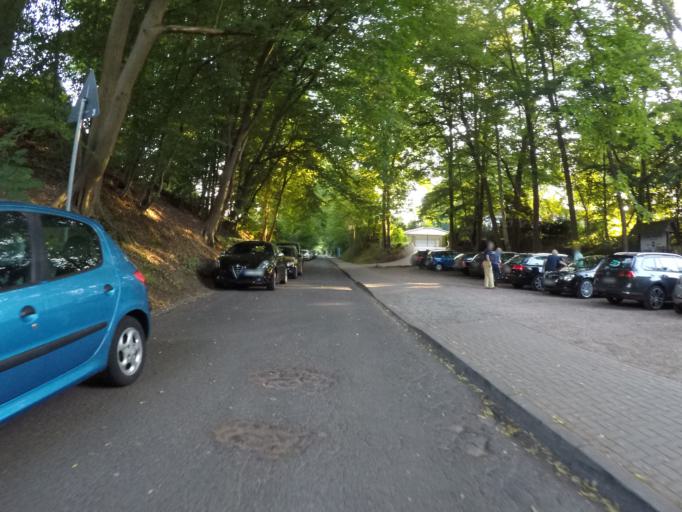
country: DE
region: Hamburg
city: Sasel
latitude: 53.6697
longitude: 10.1081
